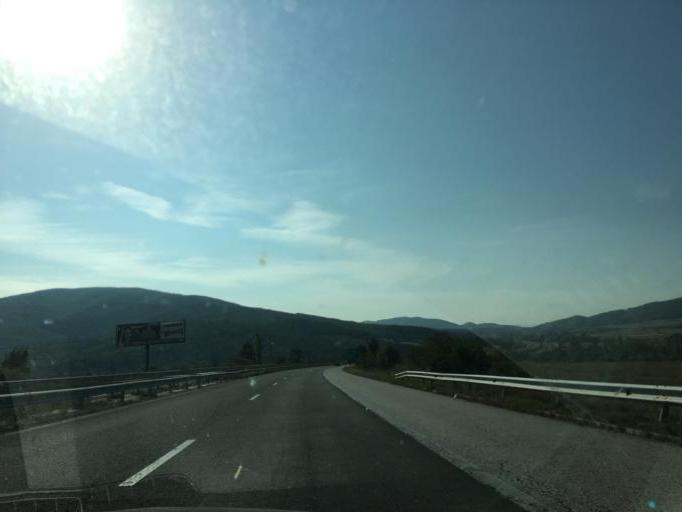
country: BG
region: Sofiya
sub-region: Obshtina Ikhtiman
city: Ikhtiman
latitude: 42.4092
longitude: 23.8640
